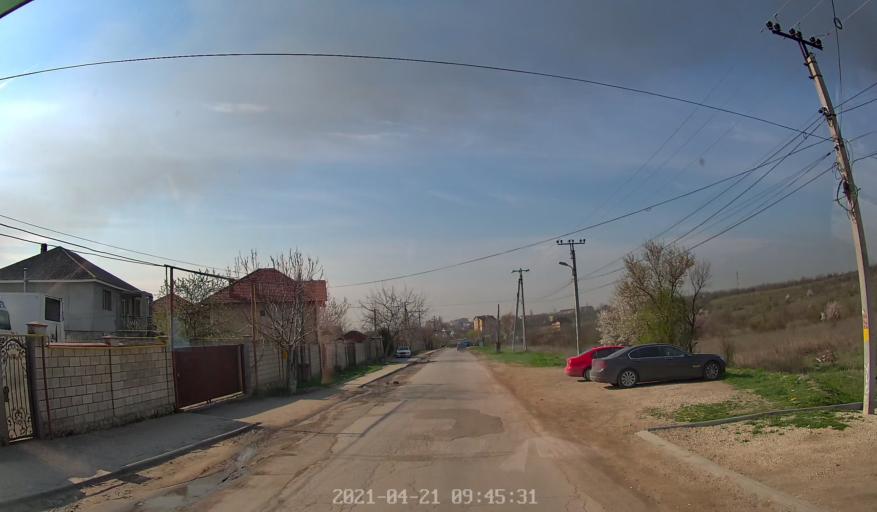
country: MD
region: Chisinau
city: Chisinau
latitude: 46.9920
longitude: 28.9344
